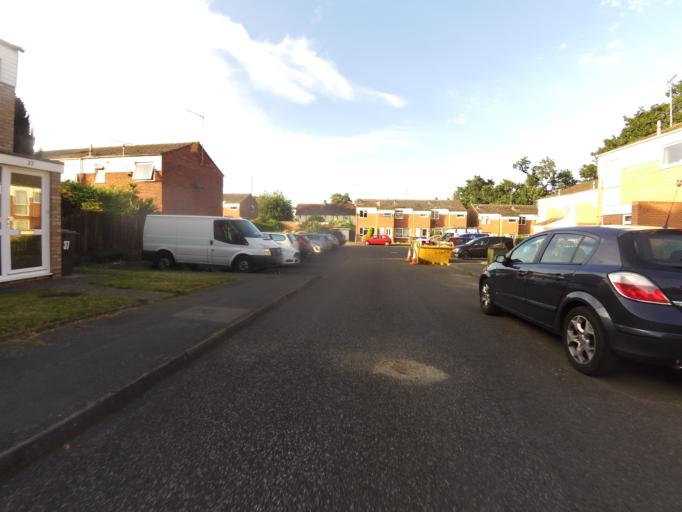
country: GB
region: England
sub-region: Suffolk
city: Ipswich
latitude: 52.0374
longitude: 1.1401
